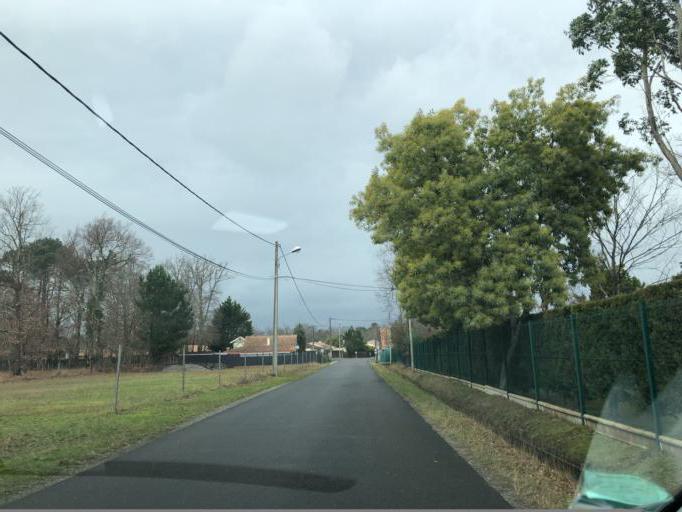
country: FR
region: Aquitaine
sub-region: Departement de la Gironde
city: Hourtin
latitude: 45.1810
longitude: -1.0756
